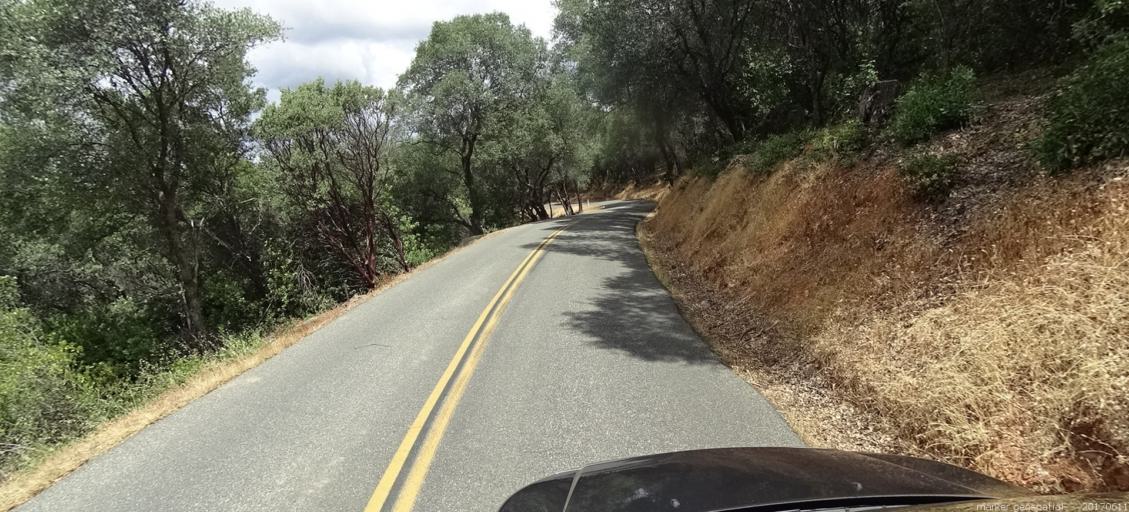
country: US
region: California
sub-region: Butte County
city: Oroville
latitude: 39.6451
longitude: -121.5481
